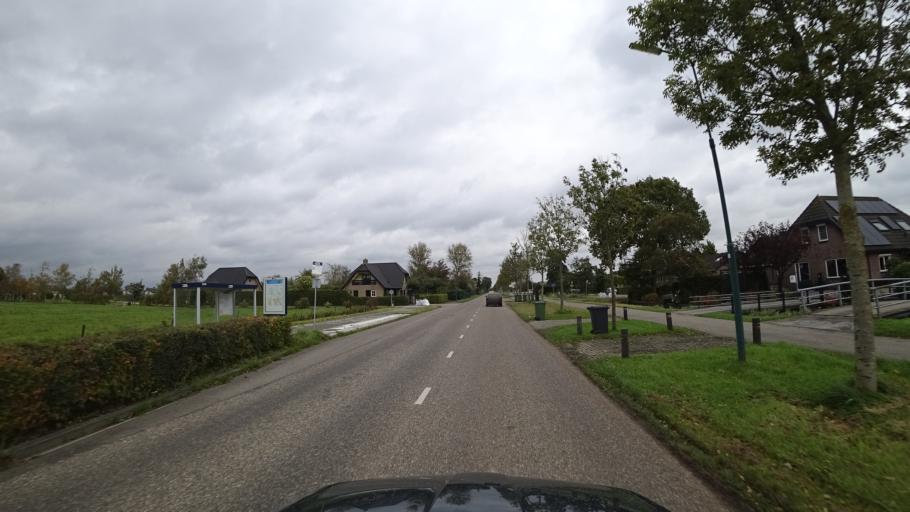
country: NL
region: Utrecht
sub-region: Stichtse Vecht
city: Maarssen
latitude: 52.1436
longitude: 5.0552
